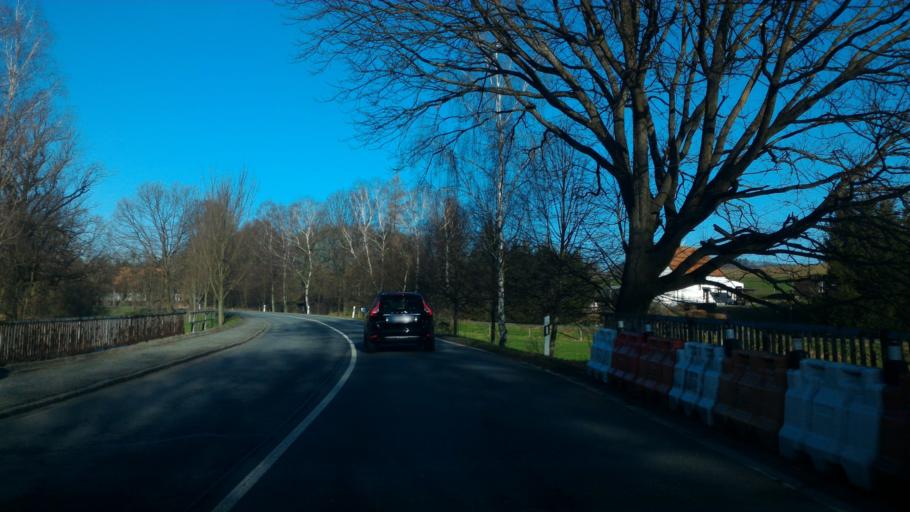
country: DE
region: Saxony
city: Neustadt in Sachsen
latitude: 51.0299
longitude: 14.2071
